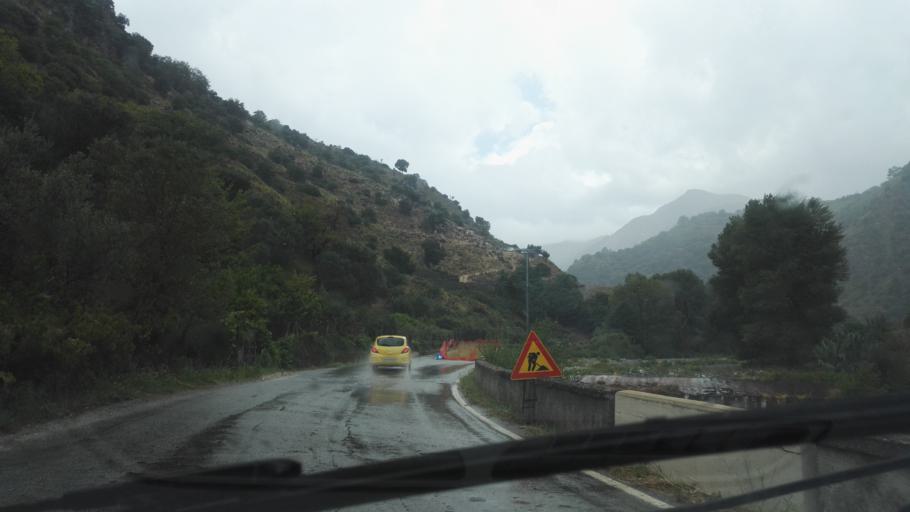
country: IT
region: Calabria
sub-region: Provincia di Reggio Calabria
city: Stilo
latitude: 38.4849
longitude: 16.4720
